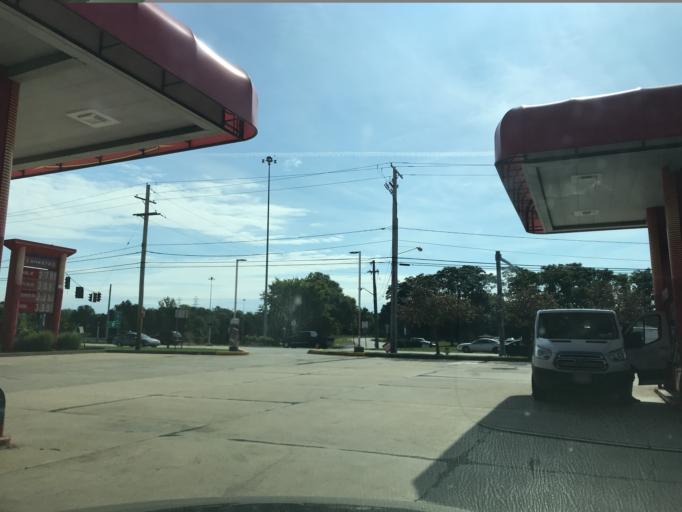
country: US
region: Ohio
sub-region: Ashtabula County
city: Edgewood
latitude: 41.8765
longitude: -80.7644
